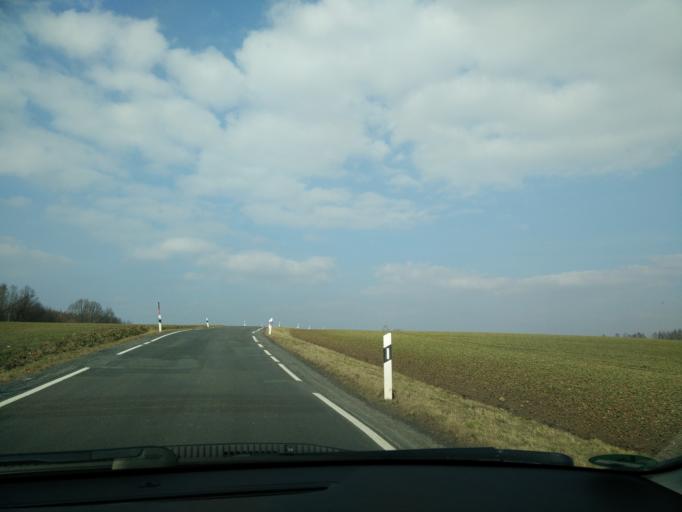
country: DE
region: Saxony
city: Colditz
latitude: 51.1076
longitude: 12.7761
